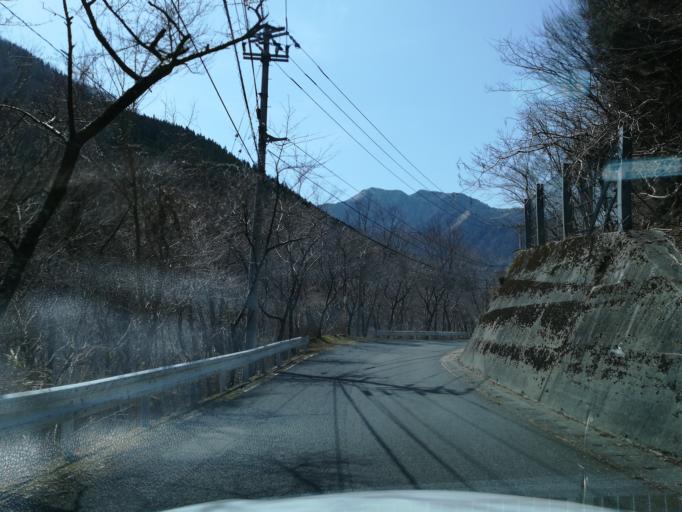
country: JP
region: Tokushima
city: Wakimachi
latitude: 33.8518
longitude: 134.0388
